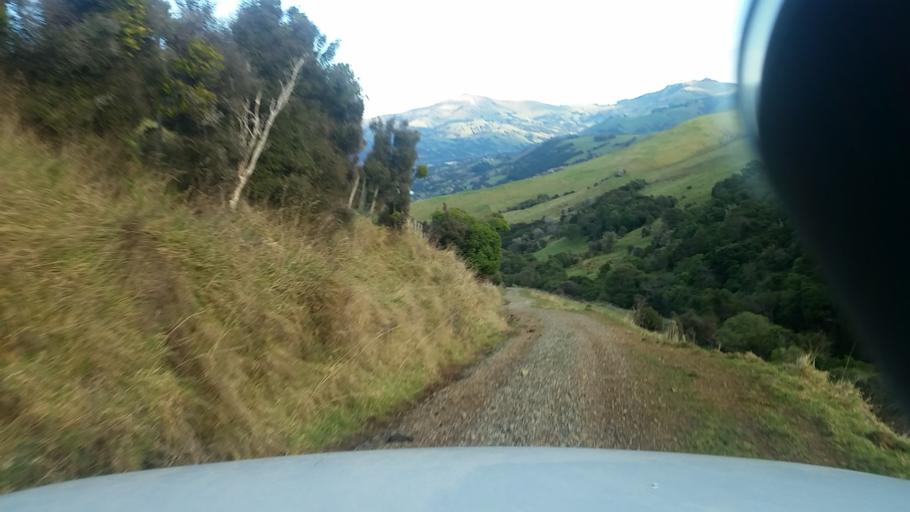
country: NZ
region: Canterbury
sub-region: Christchurch City
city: Christchurch
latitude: -43.7562
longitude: 173.0034
